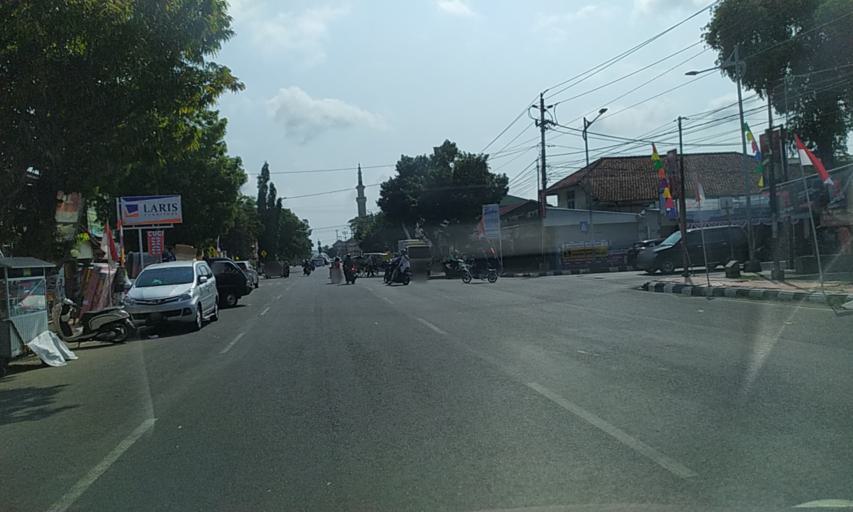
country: ID
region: Central Java
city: Karangbadar Kidul
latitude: -7.7279
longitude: 109.0115
